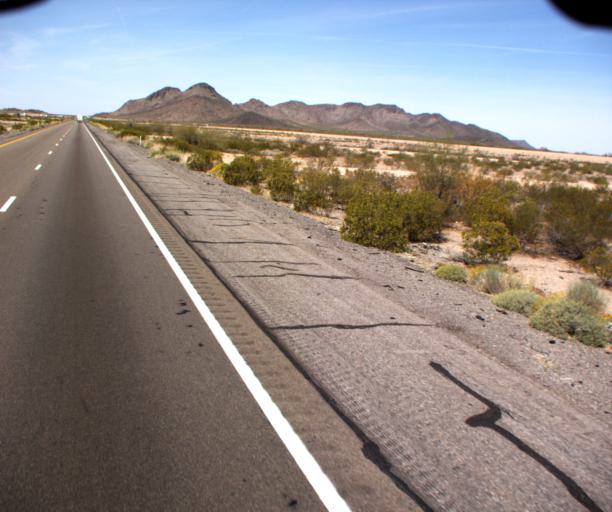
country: US
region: Arizona
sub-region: La Paz County
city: Salome
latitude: 33.6069
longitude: -113.6035
